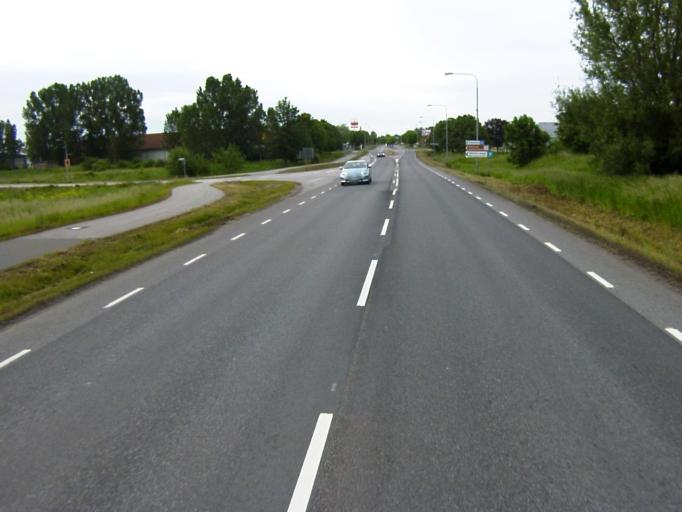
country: SE
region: Skane
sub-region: Kristianstads Kommun
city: Kristianstad
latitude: 56.0254
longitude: 14.1411
